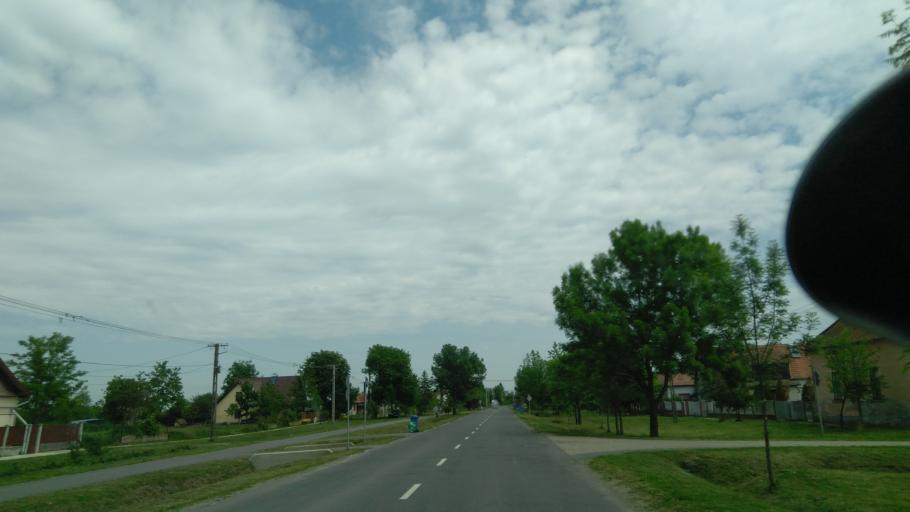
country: HU
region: Hajdu-Bihar
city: Komadi
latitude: 47.0118
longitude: 21.5051
